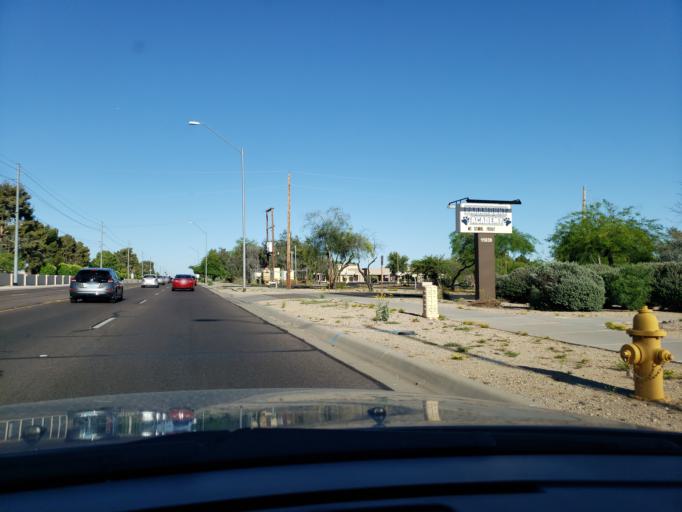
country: US
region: Arizona
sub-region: Maricopa County
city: Youngtown
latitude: 33.5655
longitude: -112.2968
